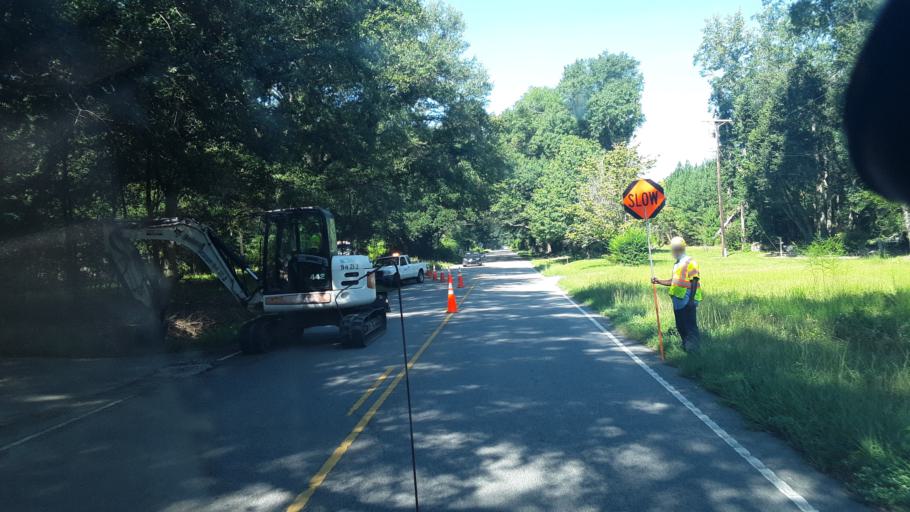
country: US
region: South Carolina
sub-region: Jasper County
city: Ridgeland
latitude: 32.5894
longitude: -80.9475
